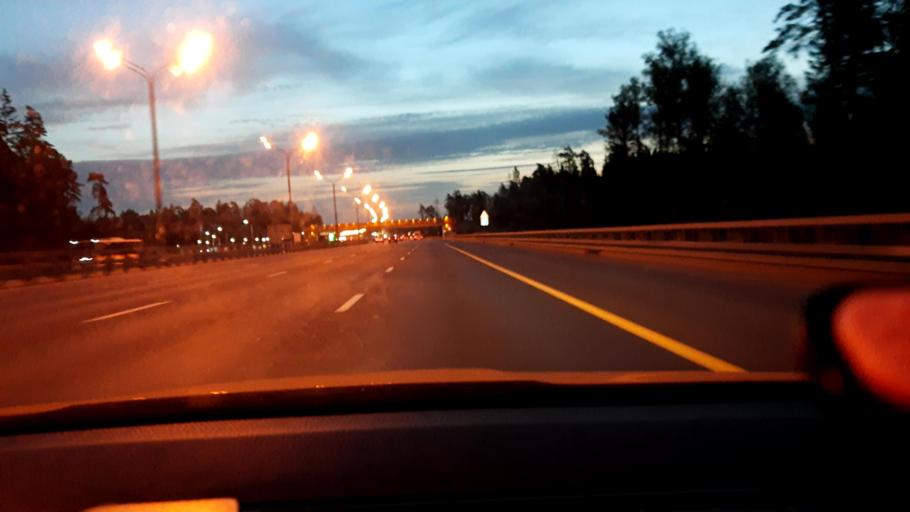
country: RU
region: Moskovskaya
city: Krasnoznamensk
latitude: 55.6093
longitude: 37.0623
